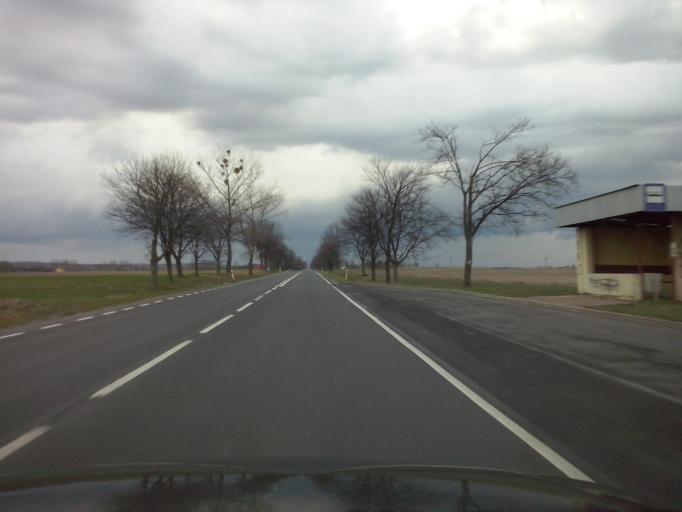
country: PL
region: Lublin Voivodeship
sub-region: Powiat chelmski
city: Rejowiec
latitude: 51.1704
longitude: 23.3173
